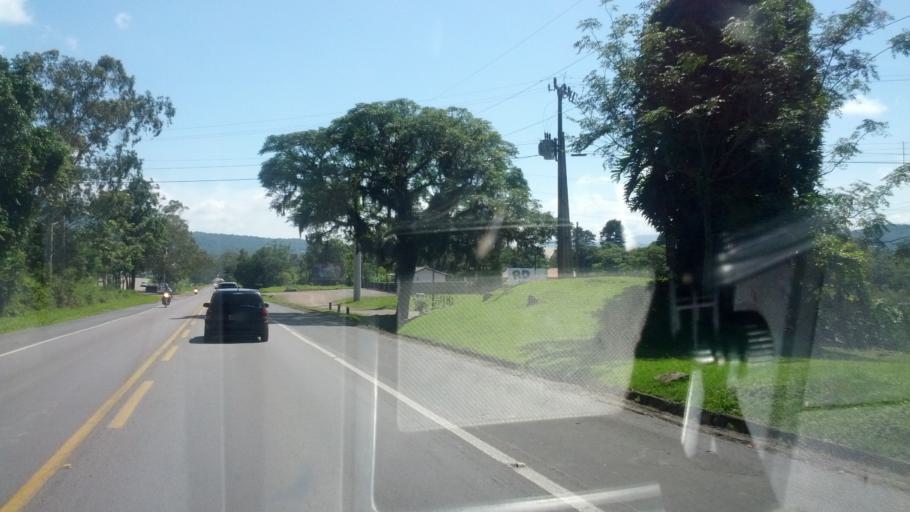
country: BR
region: Santa Catarina
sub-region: Rio Do Sul
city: Rio do Sul
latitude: -27.1844
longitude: -49.6039
